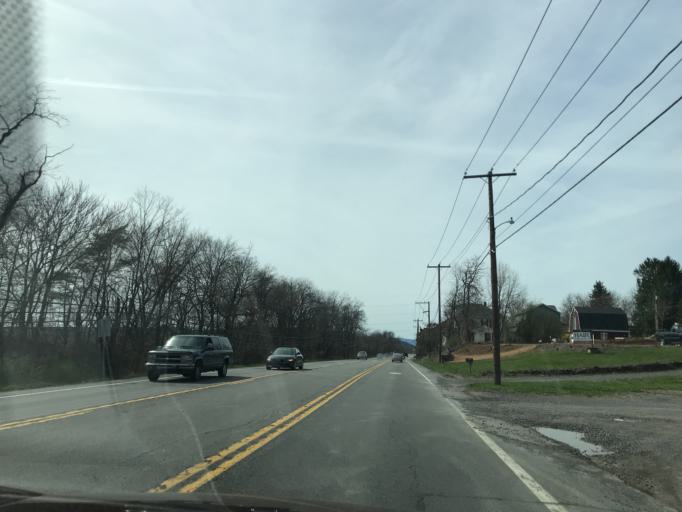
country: US
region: Pennsylvania
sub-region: Northumberland County
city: Northumberland
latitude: 40.9020
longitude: -76.8241
